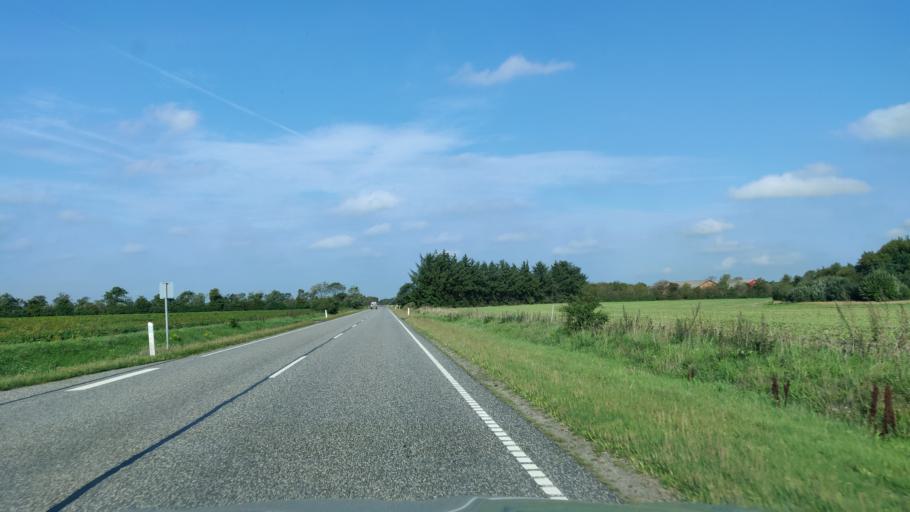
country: DK
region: Central Jutland
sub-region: Herning Kommune
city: Sunds
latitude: 56.2507
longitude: 9.0575
